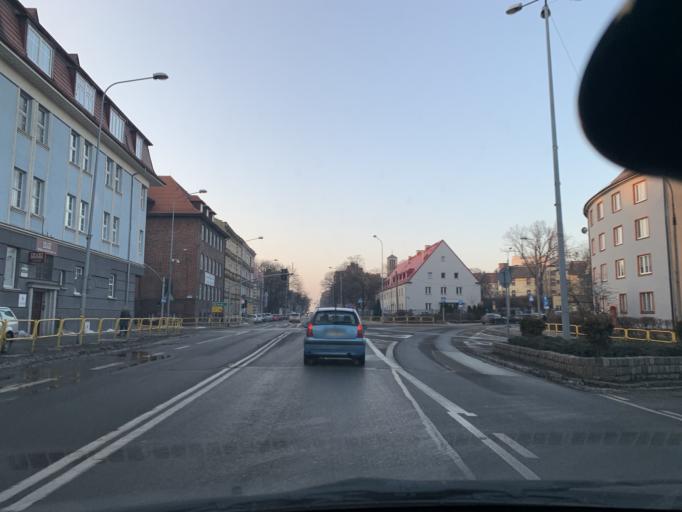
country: PL
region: Silesian Voivodeship
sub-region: Bytom
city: Bytom
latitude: 50.3513
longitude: 18.9132
